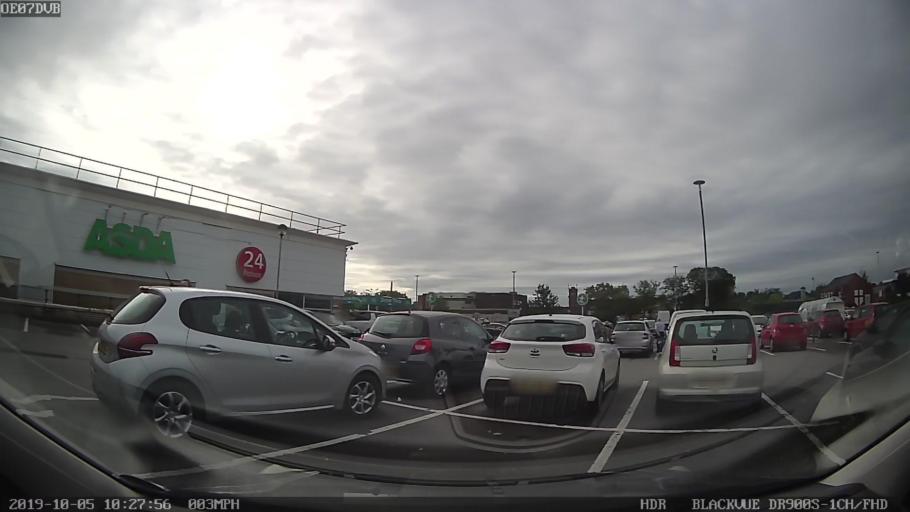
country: GB
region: England
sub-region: Borough of Oldham
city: Oldham
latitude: 53.5466
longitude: -2.1411
